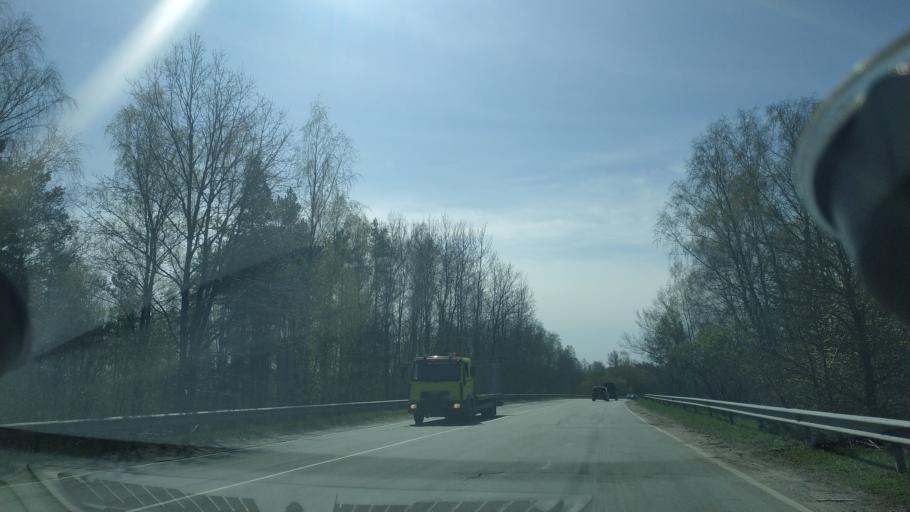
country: LT
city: Ramuciai
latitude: 54.9267
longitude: 24.0507
